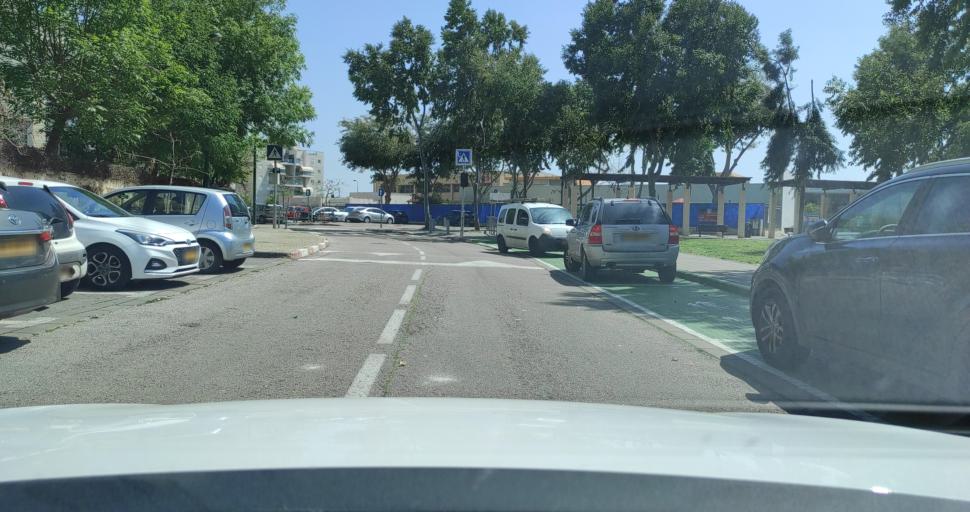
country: IL
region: Central District
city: Nordiyya
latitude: 32.2967
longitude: 34.8718
